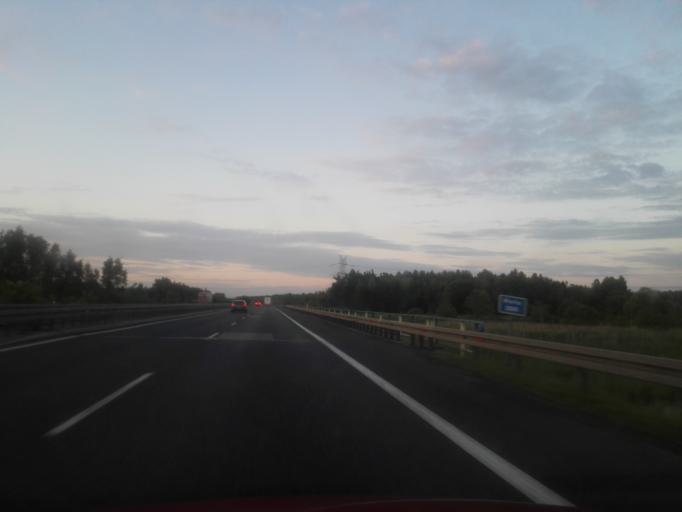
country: PL
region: Silesian Voivodeship
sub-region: Powiat czestochowski
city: Borowno
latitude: 51.0269
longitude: 19.3262
